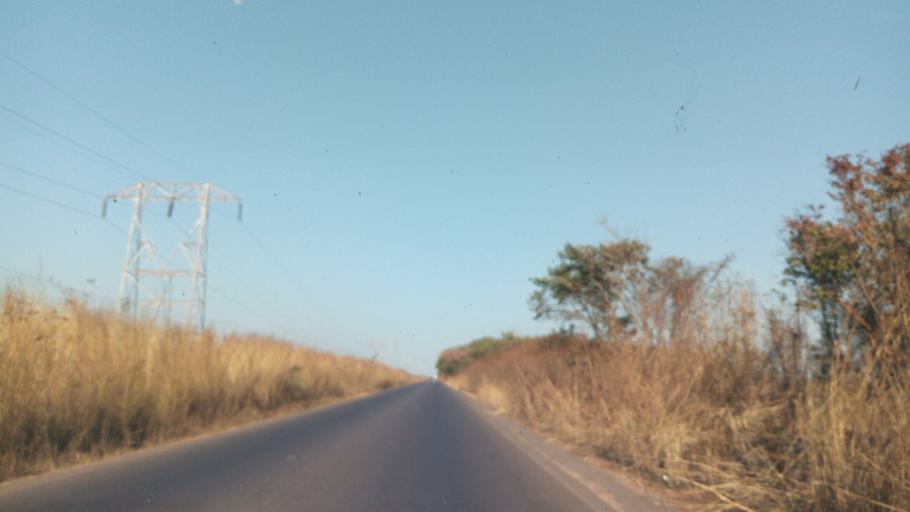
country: CD
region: Katanga
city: Likasi
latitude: -11.0035
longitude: 26.8990
